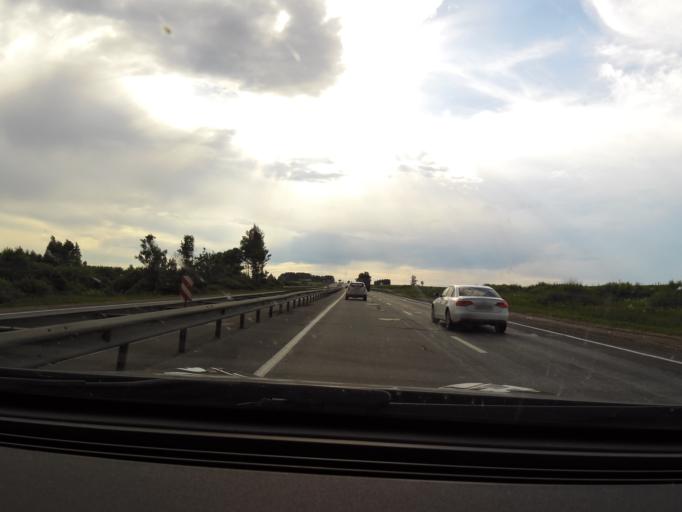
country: RU
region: Vladimir
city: Novovyazniki
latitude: 56.2169
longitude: 42.2357
